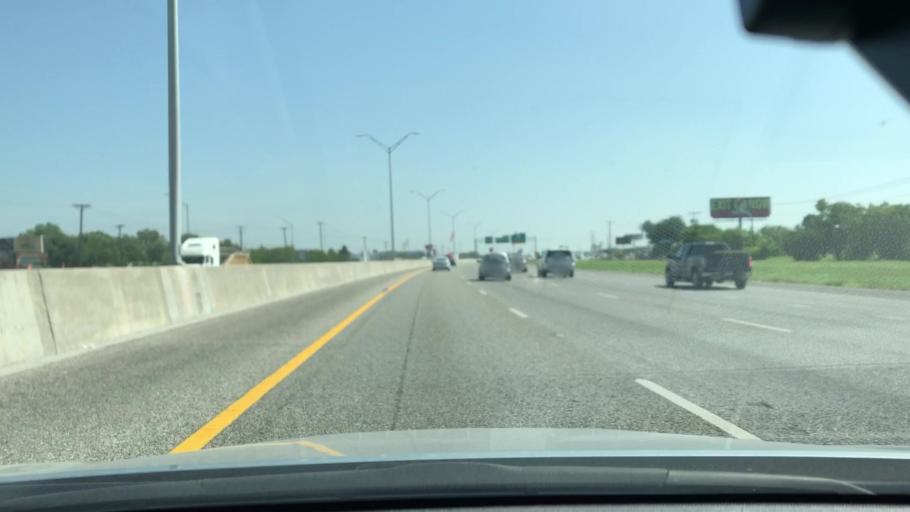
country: US
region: Texas
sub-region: Comal County
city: New Braunfels
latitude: 29.7203
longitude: -98.0876
